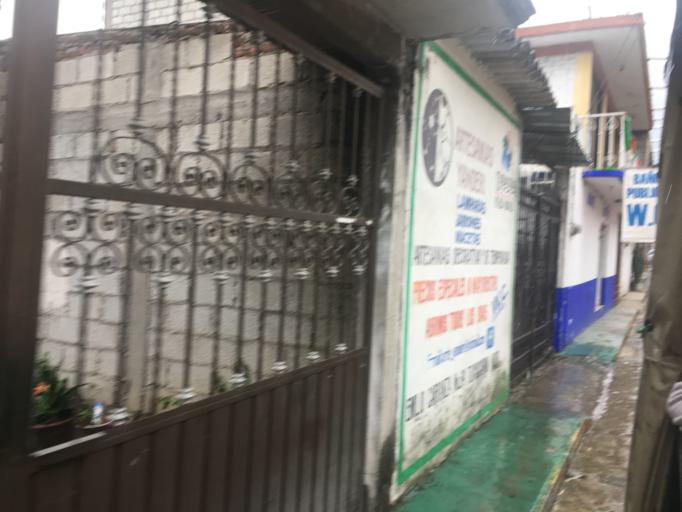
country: MX
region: Morelos
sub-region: Tlayacapan
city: Tlayacapan
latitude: 18.9541
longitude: -98.9802
